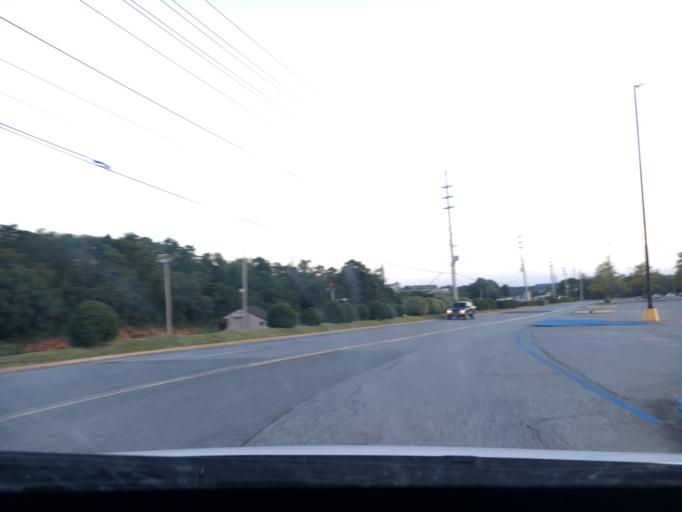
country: US
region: Virginia
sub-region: City of Lynchburg
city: West Lynchburg
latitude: 37.3655
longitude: -79.1748
